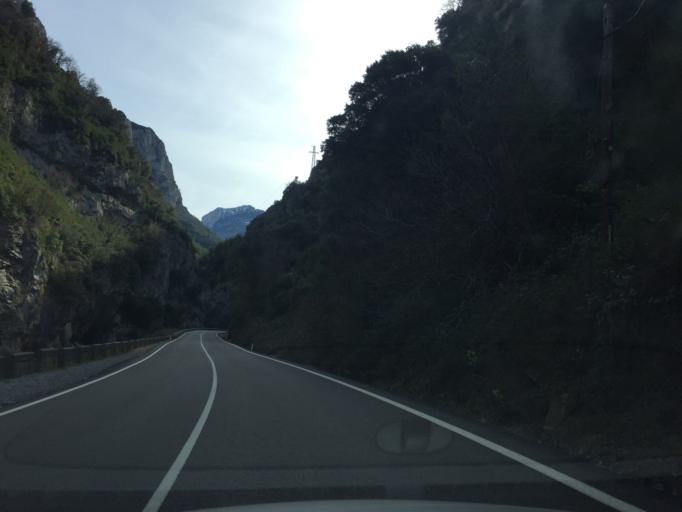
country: ES
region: Aragon
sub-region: Provincia de Huesca
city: Puertolas
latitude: 42.5610
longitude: 0.2046
